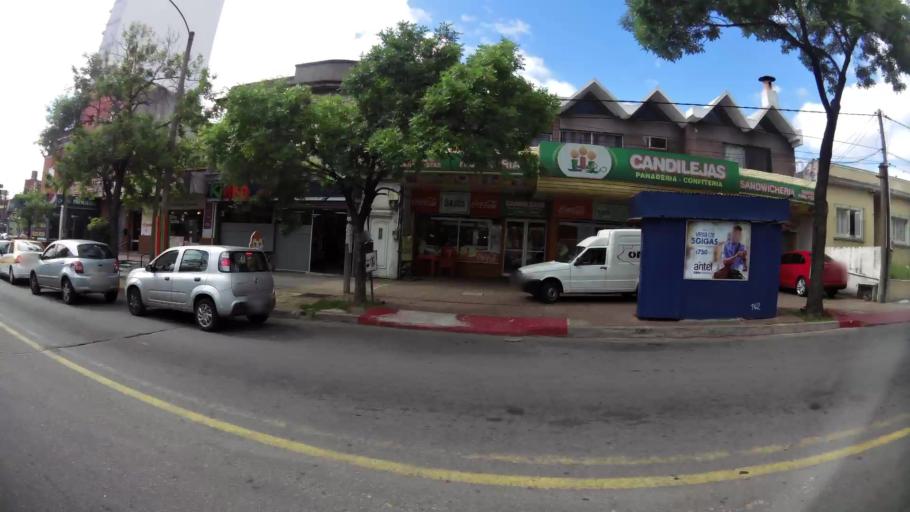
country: UY
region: Montevideo
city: Montevideo
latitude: -34.8931
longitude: -56.1304
